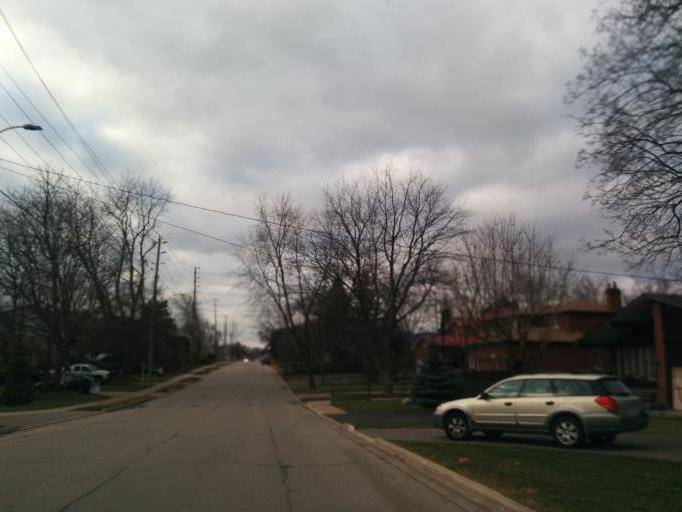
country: CA
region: Ontario
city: Etobicoke
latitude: 43.5904
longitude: -79.5701
